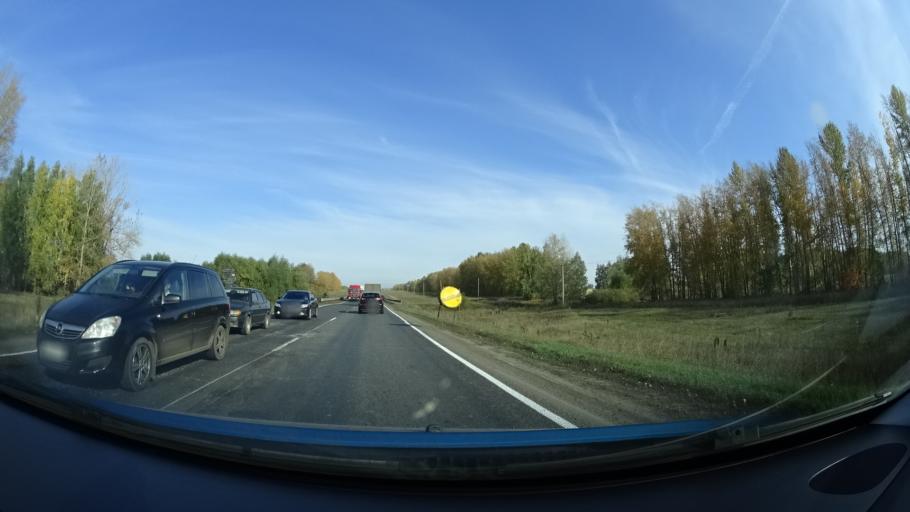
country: RU
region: Bashkortostan
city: Buzdyak
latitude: 54.6621
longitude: 54.7038
